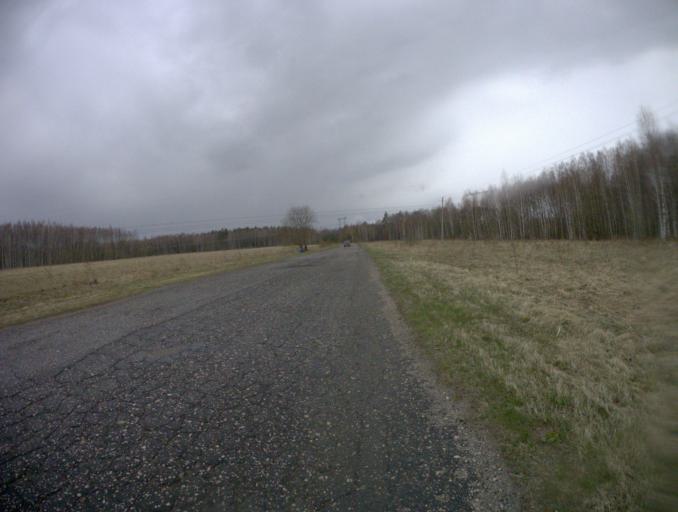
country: RU
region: Vladimir
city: Sudogda
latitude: 55.9671
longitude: 40.6916
